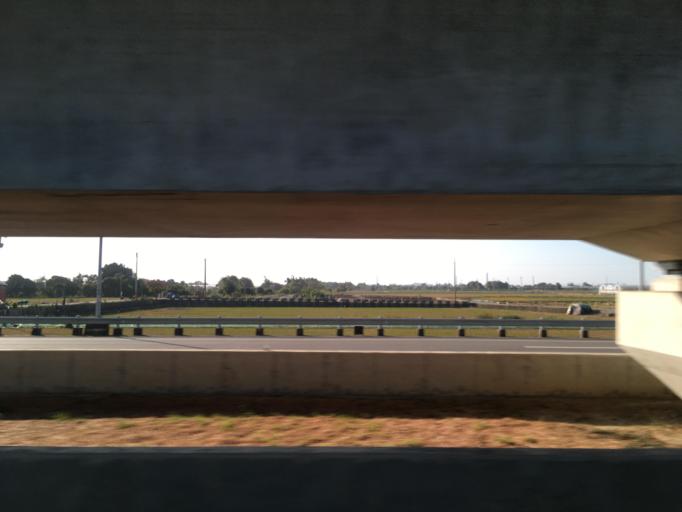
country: TW
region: Taiwan
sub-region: Chiayi
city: Taibao
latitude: 23.4374
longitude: 120.3228
